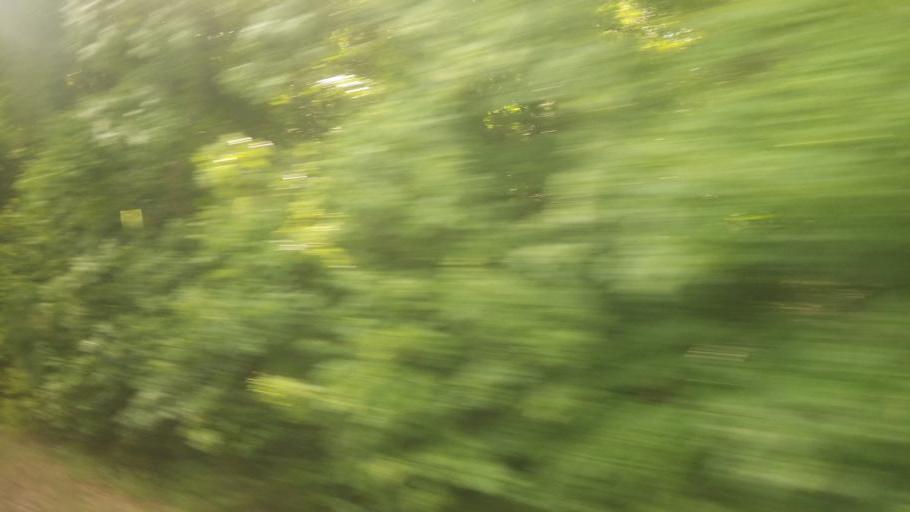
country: US
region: Kansas
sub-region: Wyandotte County
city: Bonner Springs
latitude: 39.0021
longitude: -94.8973
